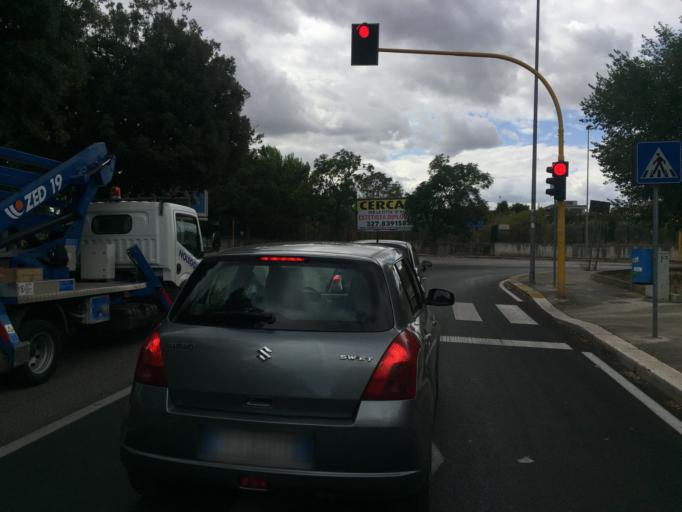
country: IT
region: Apulia
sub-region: Provincia di Bari
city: Bari
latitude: 41.0916
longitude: 16.8640
